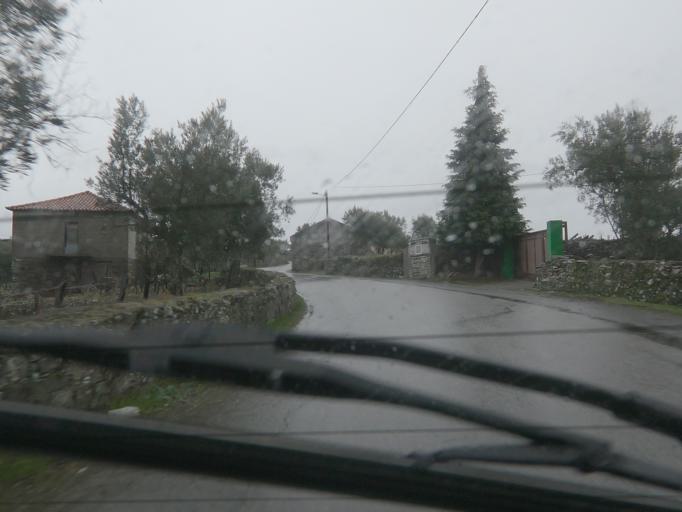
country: PT
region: Vila Real
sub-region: Peso da Regua
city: Peso da Regua
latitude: 41.1994
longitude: -7.7048
